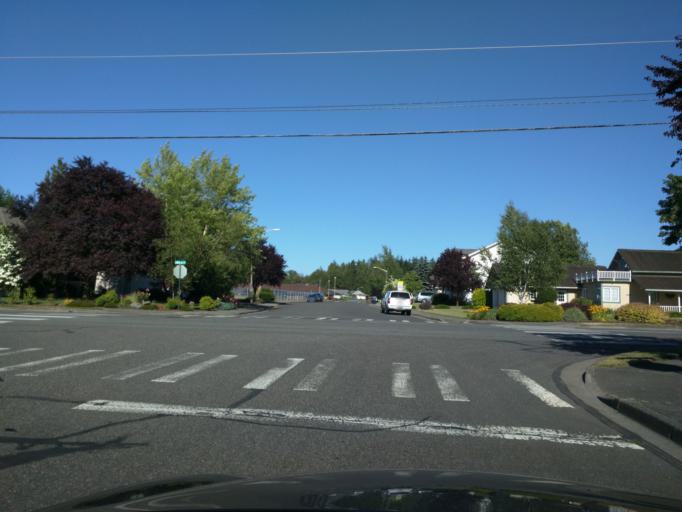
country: US
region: Washington
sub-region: Whatcom County
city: Lynden
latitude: 48.9582
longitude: -122.4302
